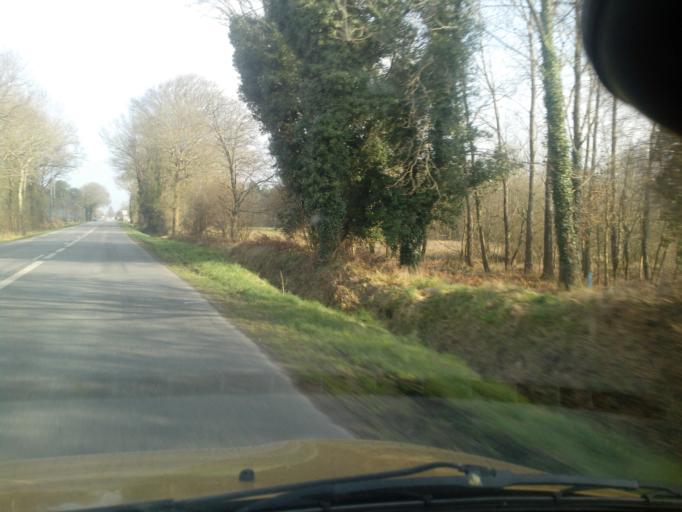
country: FR
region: Brittany
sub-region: Departement du Morbihan
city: Questembert
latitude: 47.6883
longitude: -2.4661
